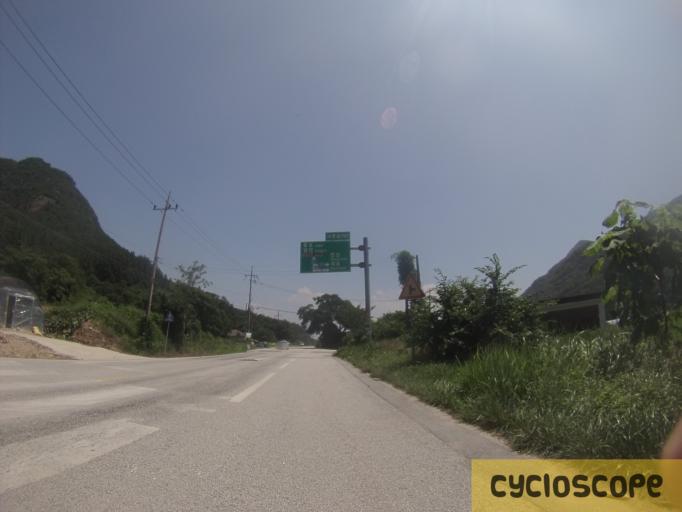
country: KR
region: Jeollabuk-do
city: Puan
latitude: 35.6639
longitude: 126.5272
